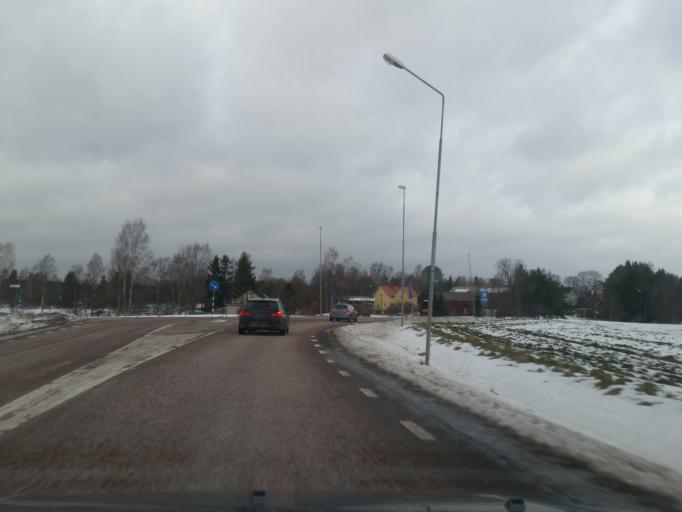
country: SE
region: Gaevleborg
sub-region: Sandvikens Kommun
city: Jarbo
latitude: 60.6979
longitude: 16.6183
